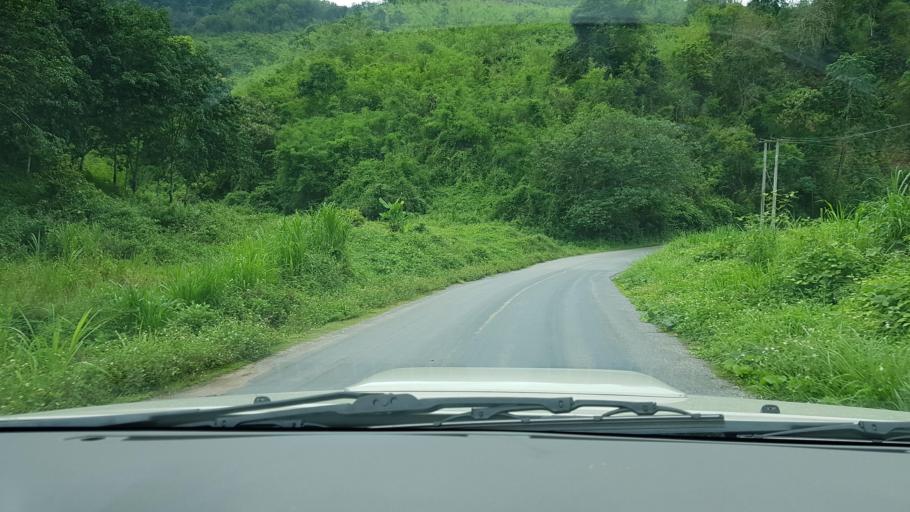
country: LA
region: Loungnamtha
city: Muang Nale
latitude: 20.3690
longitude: 101.7189
